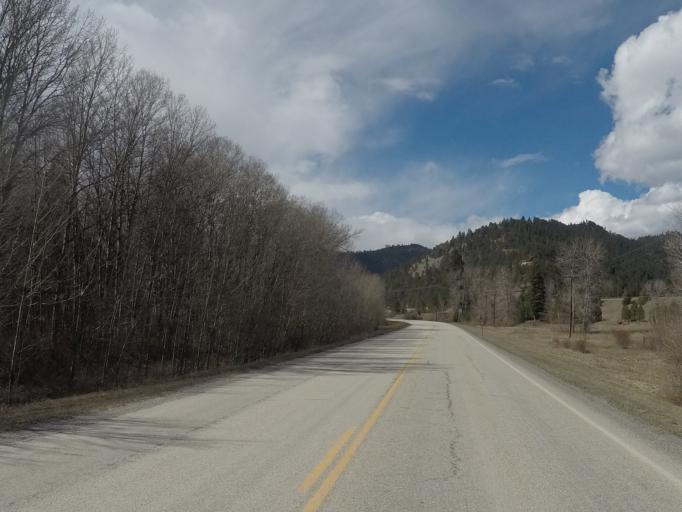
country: US
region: Montana
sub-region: Missoula County
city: Lolo
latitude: 46.7568
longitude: -114.1132
